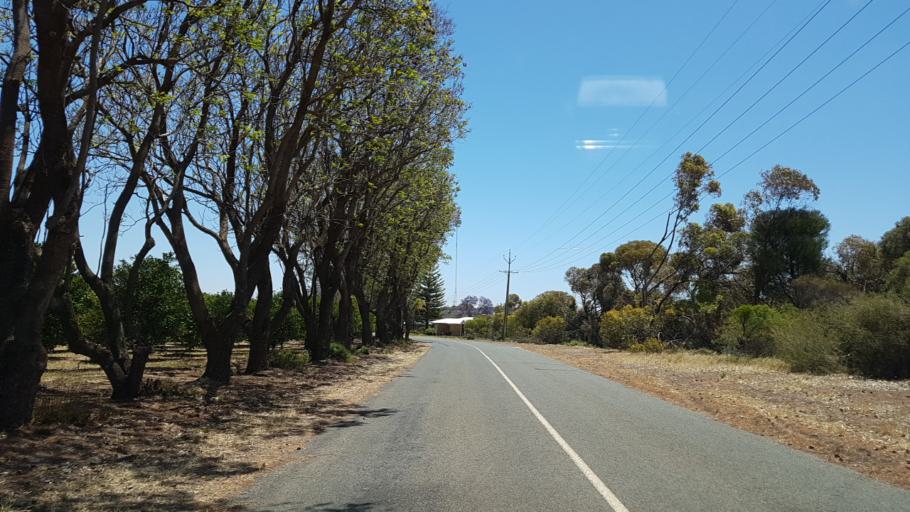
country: AU
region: South Australia
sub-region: Loxton Waikerie
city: Waikerie
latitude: -34.1676
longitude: 140.0366
